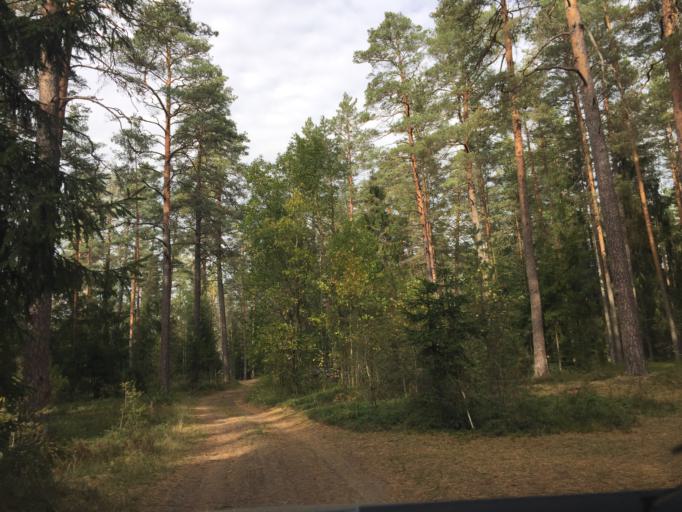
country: LV
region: Garkalne
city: Garkalne
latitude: 56.9479
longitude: 24.4298
